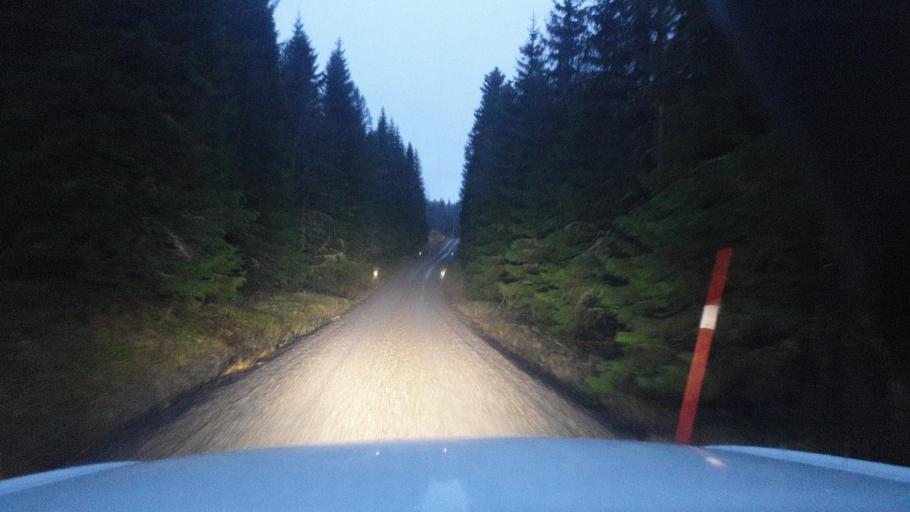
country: SE
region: Vaermland
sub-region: Eda Kommun
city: Charlottenberg
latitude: 60.0662
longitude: 12.6248
